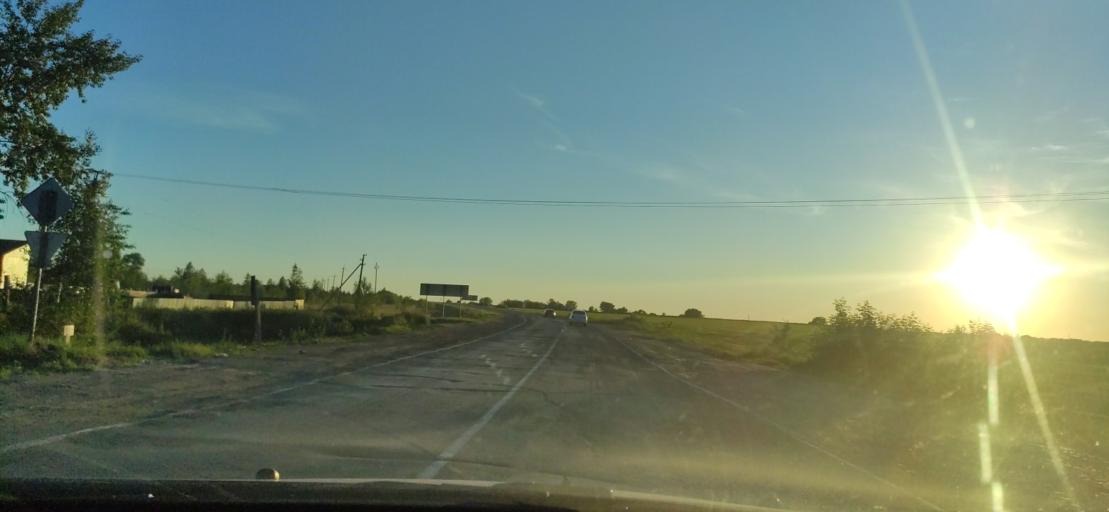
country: RU
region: Ulyanovsk
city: Cherdakly
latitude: 54.3850
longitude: 48.8430
